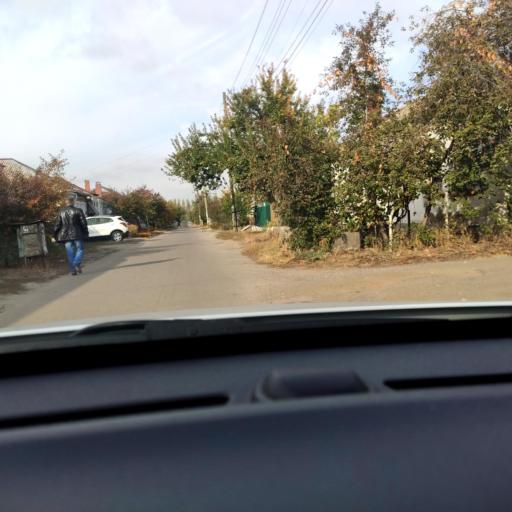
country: RU
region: Voronezj
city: Voronezh
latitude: 51.6312
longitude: 39.1661
